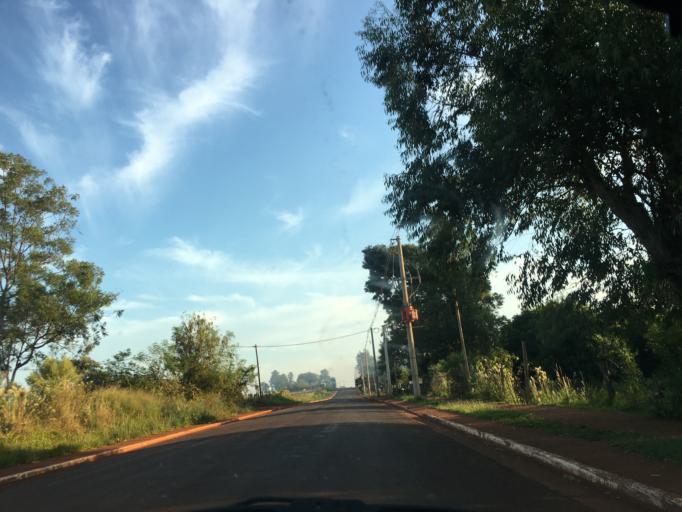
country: AR
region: Misiones
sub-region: Departamento de Capital
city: Posadas
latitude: -27.4485
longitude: -55.9336
